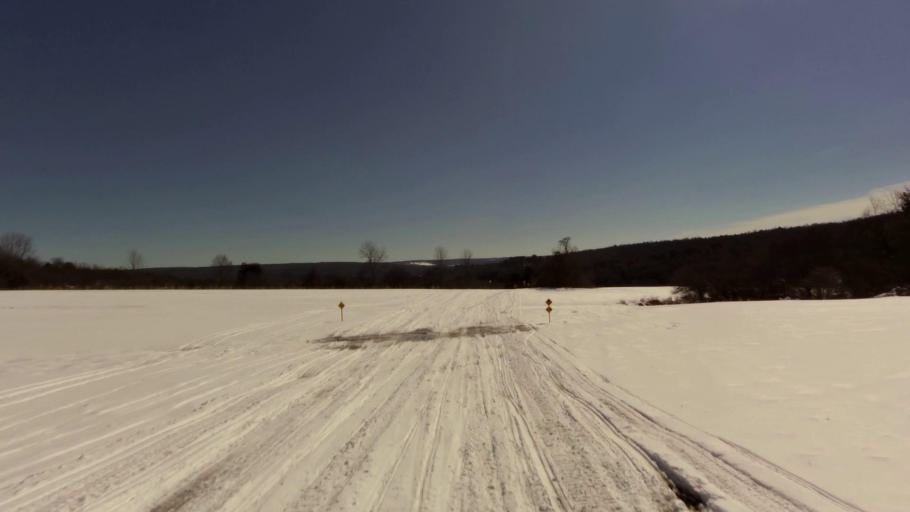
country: US
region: New York
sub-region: Allegany County
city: Houghton
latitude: 42.3620
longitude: -78.1530
